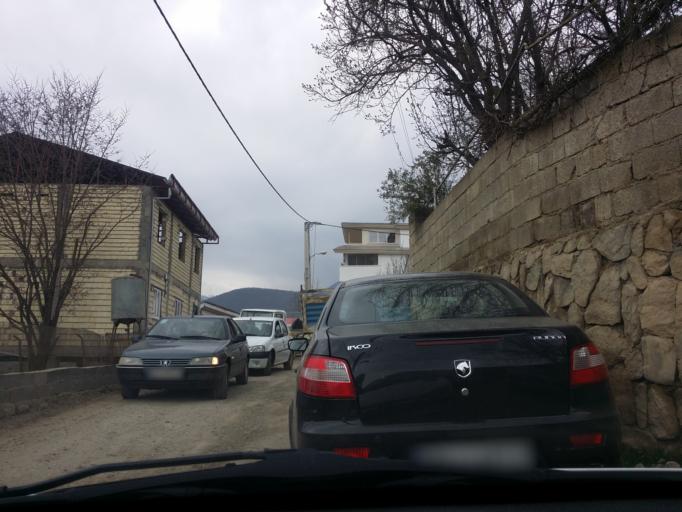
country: IR
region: Mazandaran
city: `Abbasabad
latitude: 36.5343
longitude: 51.1602
